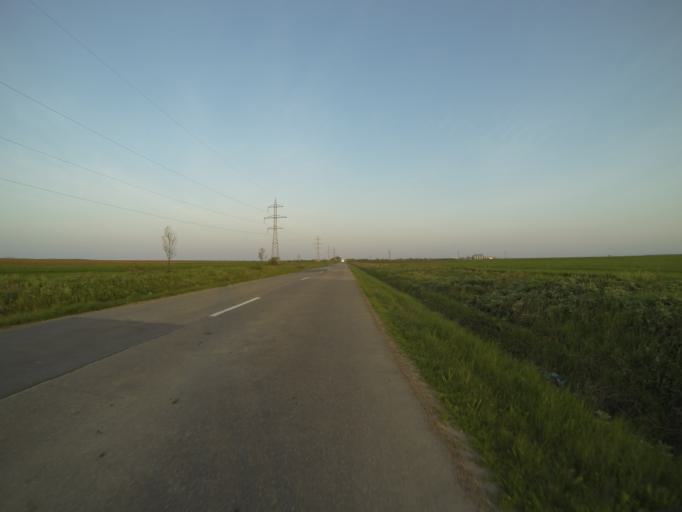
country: RO
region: Dolj
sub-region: Comuna Dranicu
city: Dranic
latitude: 44.0622
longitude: 23.8218
